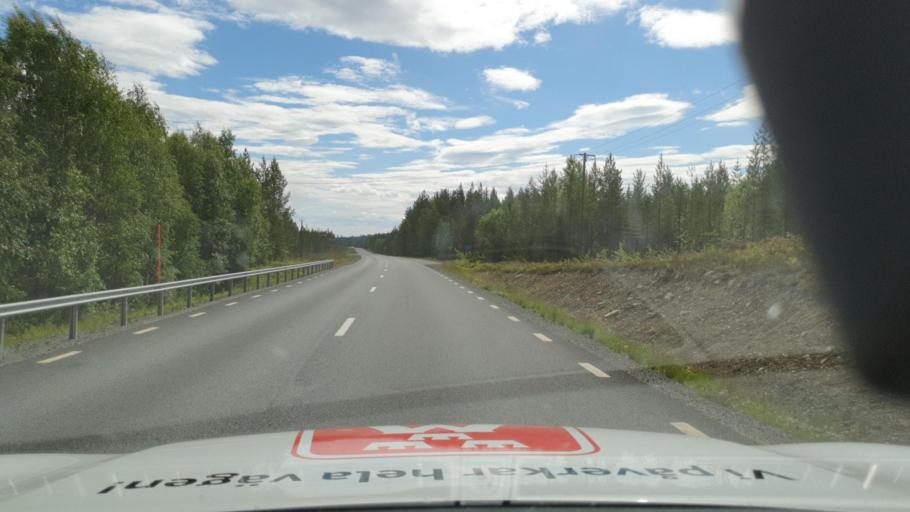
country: SE
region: Vaesterbotten
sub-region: Norsjo Kommun
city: Norsjoe
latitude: 65.1546
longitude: 19.5124
